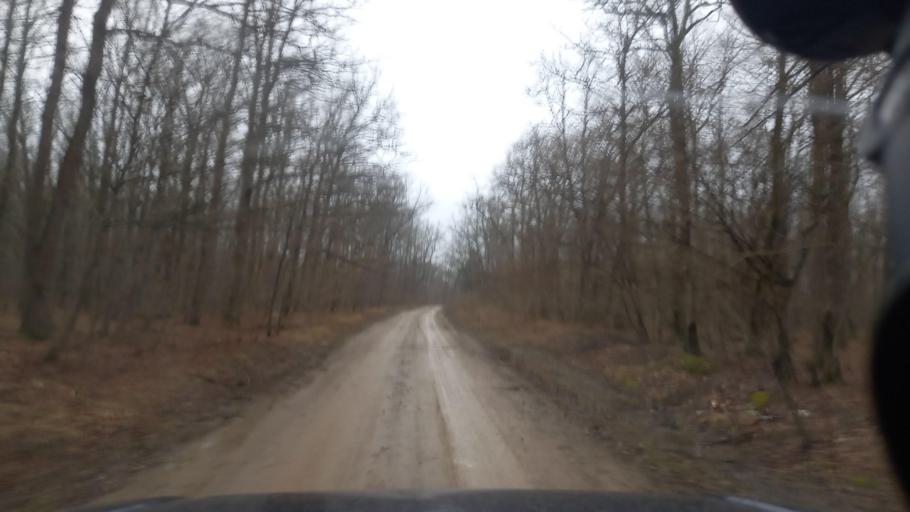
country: RU
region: Krasnodarskiy
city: Saratovskaya
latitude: 44.6628
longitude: 39.2258
